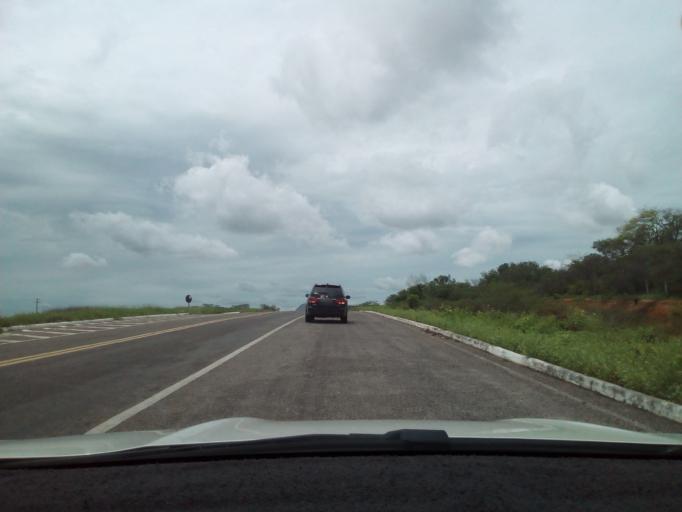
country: BR
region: Rio Grande do Norte
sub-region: Patu
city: Patu
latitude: -6.1473
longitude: -37.7479
